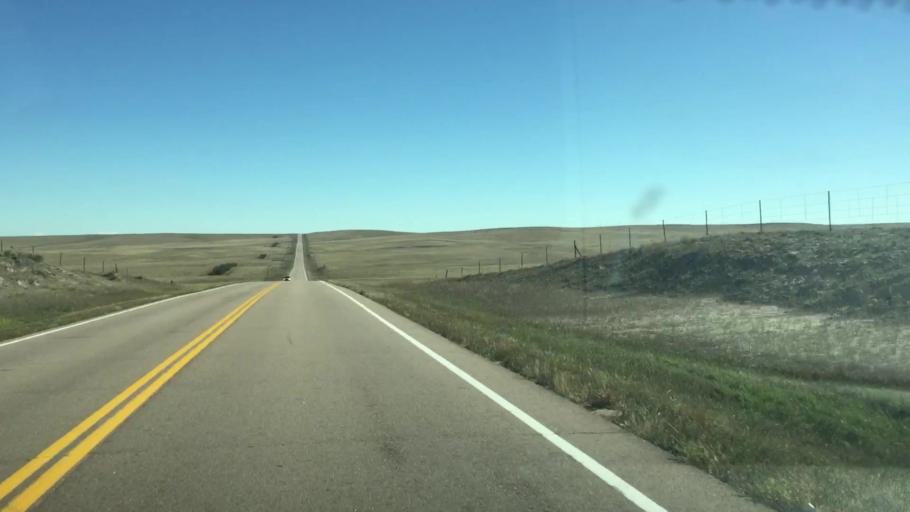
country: US
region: Colorado
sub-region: Lincoln County
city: Limon
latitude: 39.2773
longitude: -103.9998
